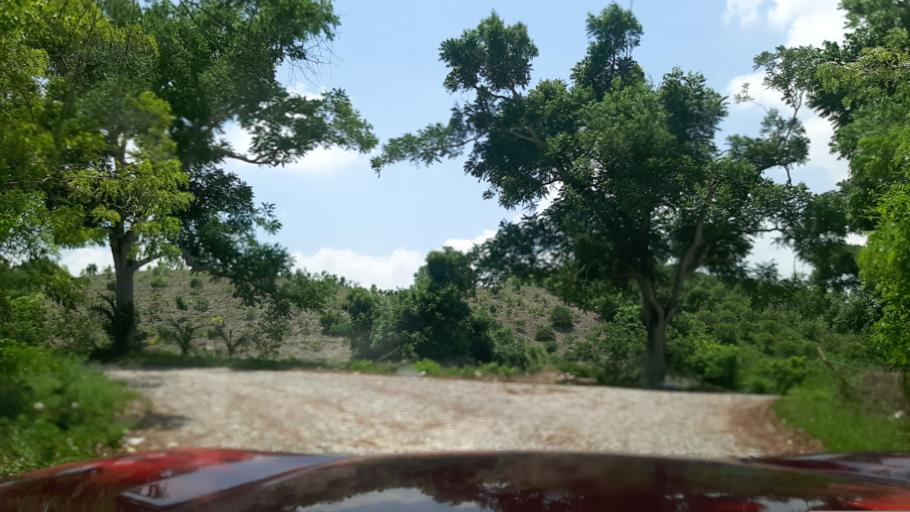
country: MX
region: Veracruz
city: Papantla de Olarte
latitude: 20.4248
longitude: -97.2694
